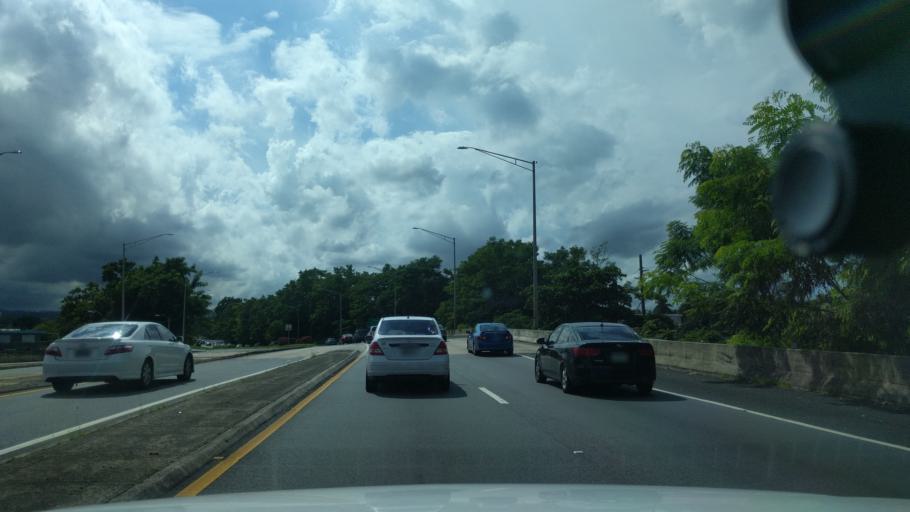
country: PR
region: Bayamon
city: Bayamon
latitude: 18.3738
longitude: -66.1643
